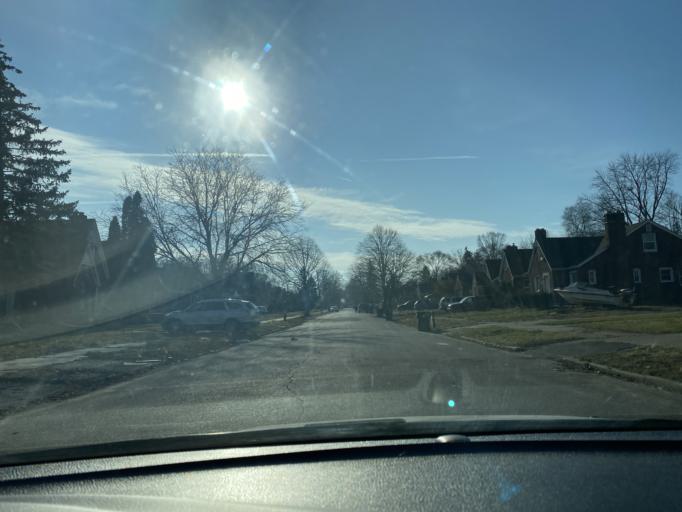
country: US
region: Michigan
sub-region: Wayne County
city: Harper Woods
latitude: 42.4133
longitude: -82.9511
